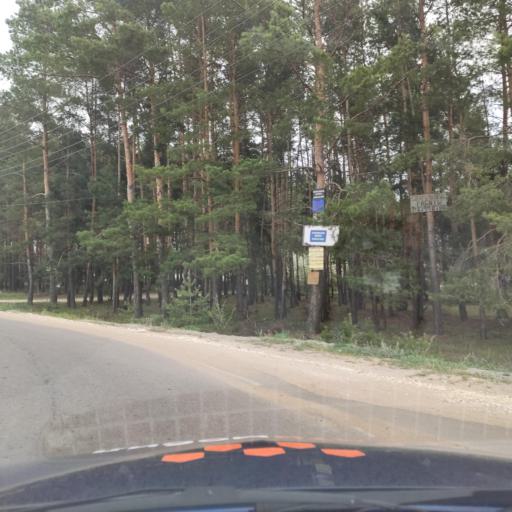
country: RU
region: Voronezj
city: Podgornoye
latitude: 51.8524
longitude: 39.1552
